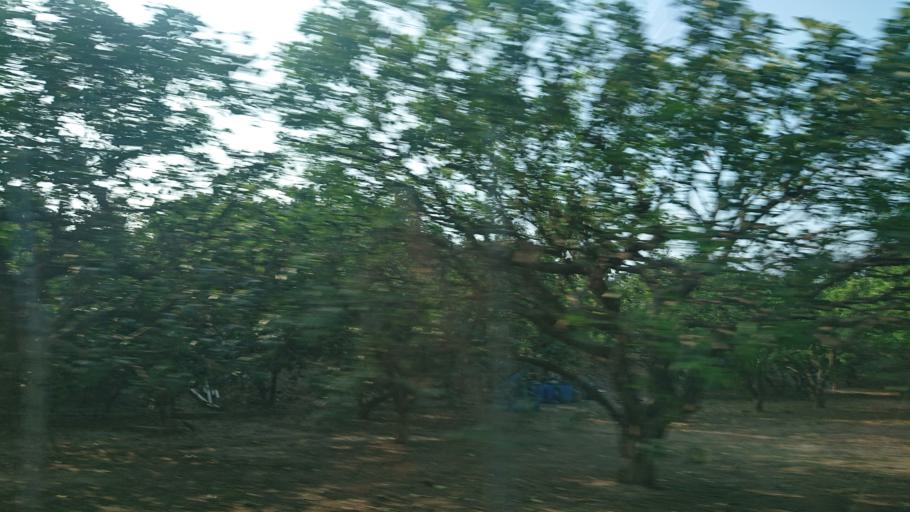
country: TW
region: Taiwan
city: Xinying
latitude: 23.1625
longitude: 120.2507
